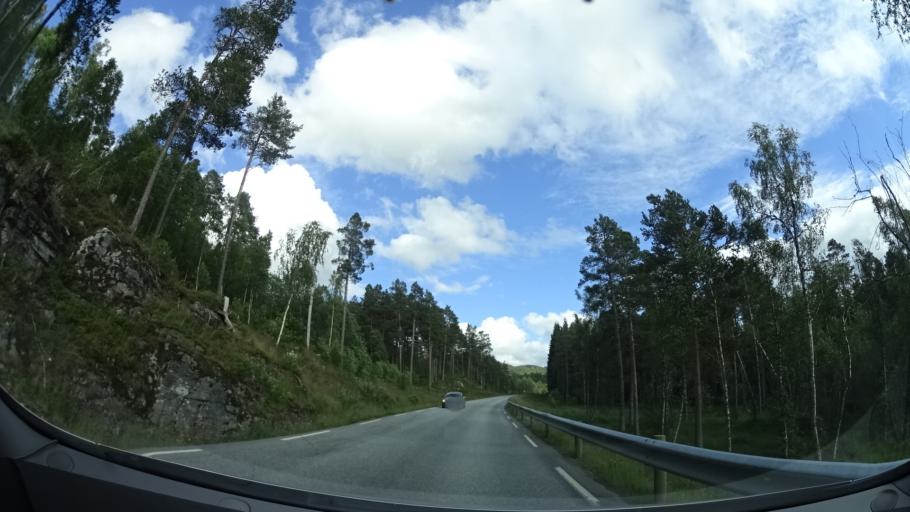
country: NO
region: More og Romsdal
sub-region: Halsa
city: Liaboen
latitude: 63.1085
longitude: 8.3338
